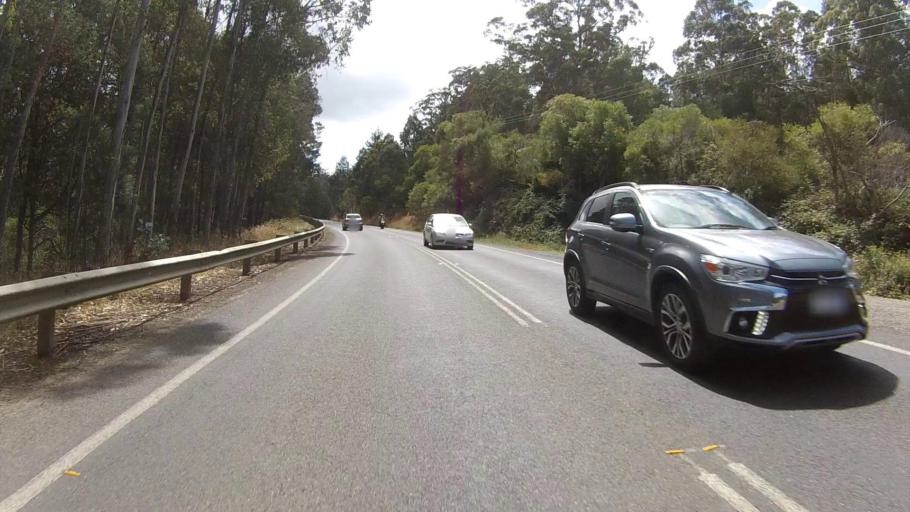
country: AU
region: Tasmania
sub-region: Kingborough
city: Kettering
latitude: -43.1046
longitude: 147.2454
